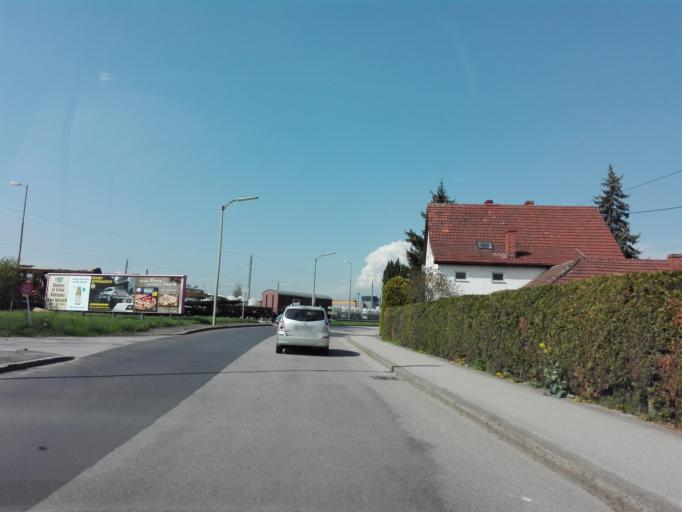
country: AT
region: Upper Austria
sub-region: Politischer Bezirk Linz-Land
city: Ansfelden
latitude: 48.2467
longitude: 14.2765
